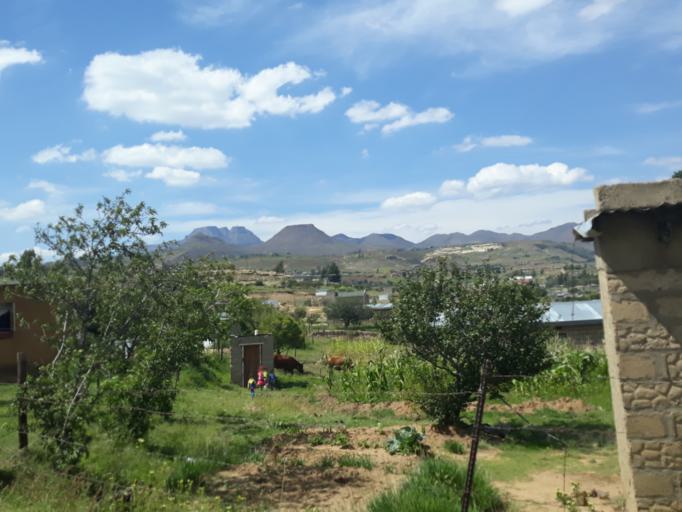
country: LS
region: Mohale's Hoek District
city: Mohale's Hoek
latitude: -30.1032
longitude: 27.4638
